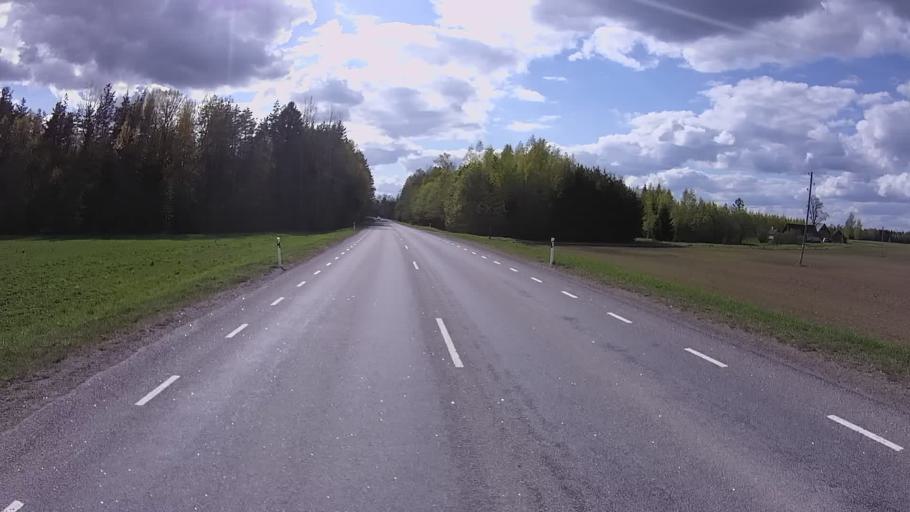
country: EE
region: Tartu
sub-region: Alatskivi vald
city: Kallaste
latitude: 58.5288
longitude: 27.0208
